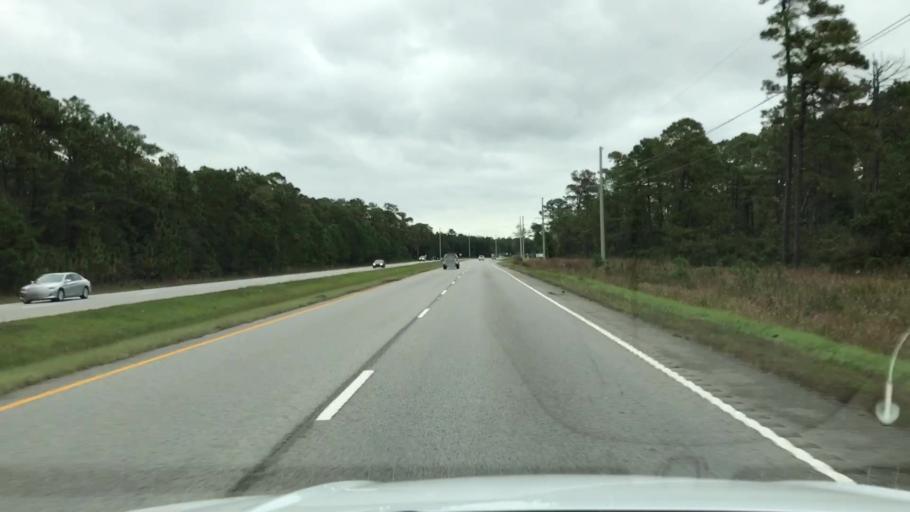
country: US
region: South Carolina
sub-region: Georgetown County
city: Georgetown
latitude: 33.4163
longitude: -79.1830
